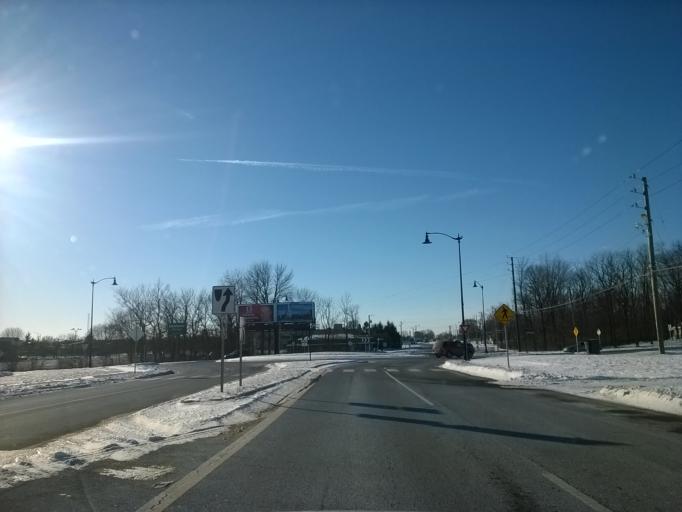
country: US
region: Indiana
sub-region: Boone County
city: Zionsville
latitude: 39.9263
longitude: -86.2212
